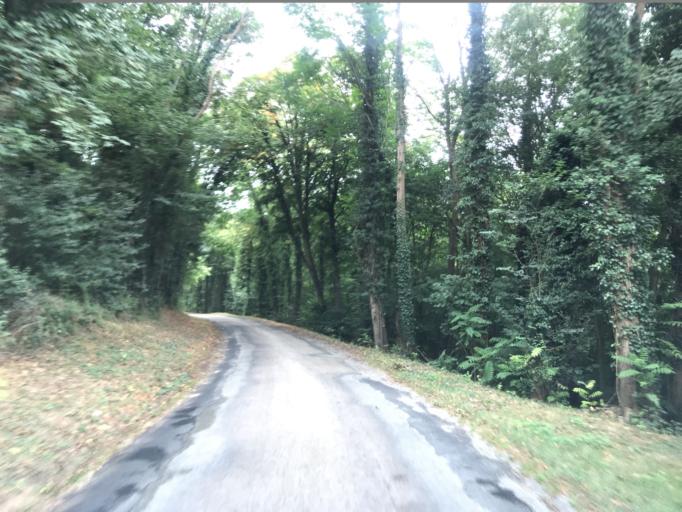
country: FR
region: Haute-Normandie
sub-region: Departement de l'Eure
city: Houlbec-Cocherel
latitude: 49.0622
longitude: 1.3362
